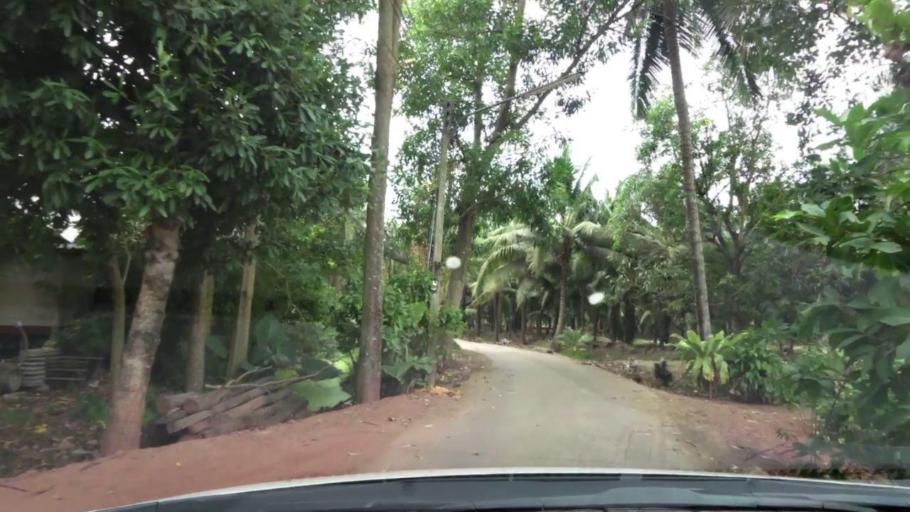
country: TH
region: Ratchaburi
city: Damnoen Saduak
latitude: 13.5756
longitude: 99.9786
